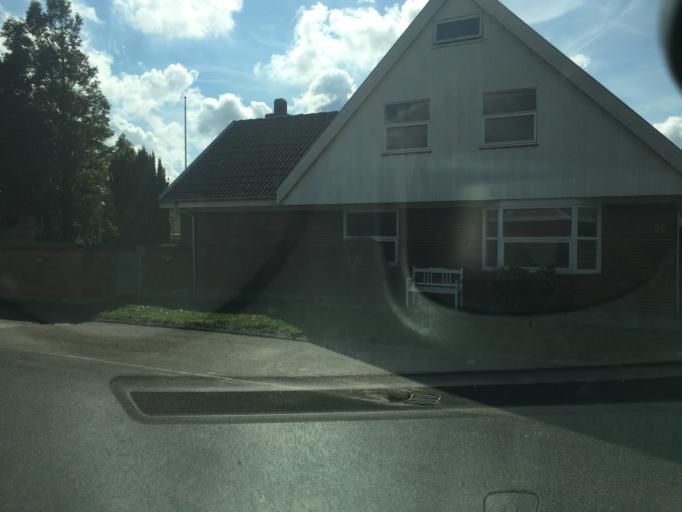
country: DK
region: South Denmark
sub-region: Tonder Kommune
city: Tonder
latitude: 54.9385
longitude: 8.8534
